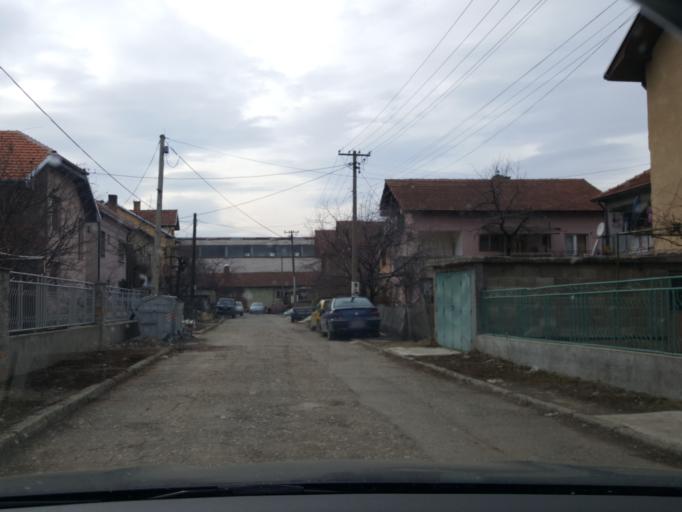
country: RS
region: Central Serbia
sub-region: Pirotski Okrug
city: Dimitrovgrad
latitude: 43.0137
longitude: 22.7697
